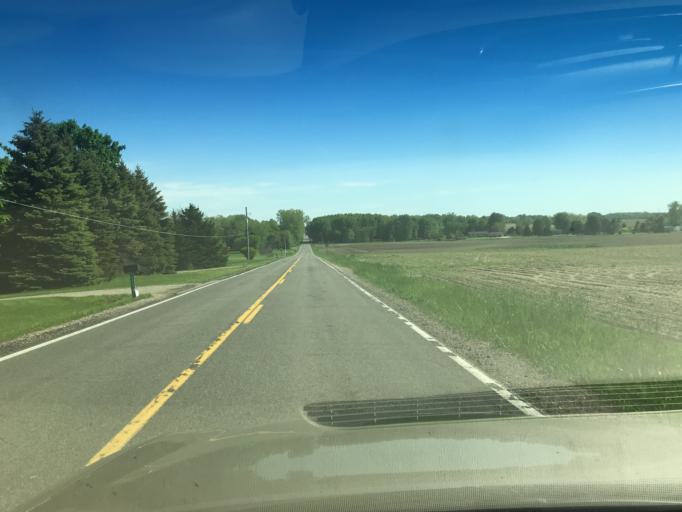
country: US
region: Michigan
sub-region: Ingham County
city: Mason
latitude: 42.5502
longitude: -84.4626
